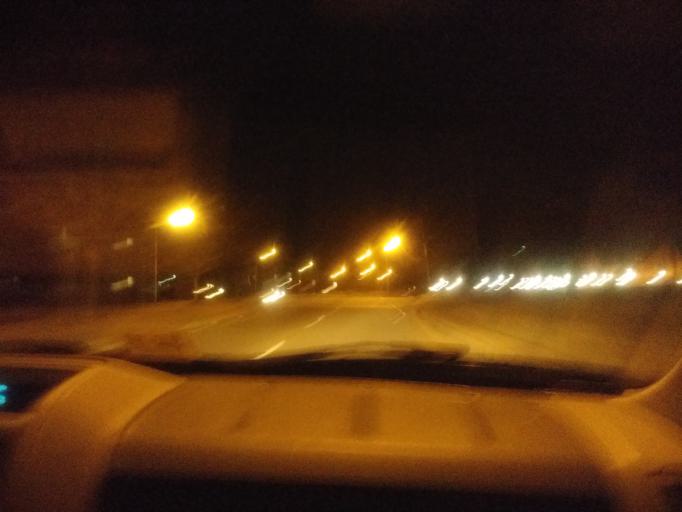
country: US
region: Virginia
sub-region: City of Chesapeake
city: Chesapeake
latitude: 36.8022
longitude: -76.1878
